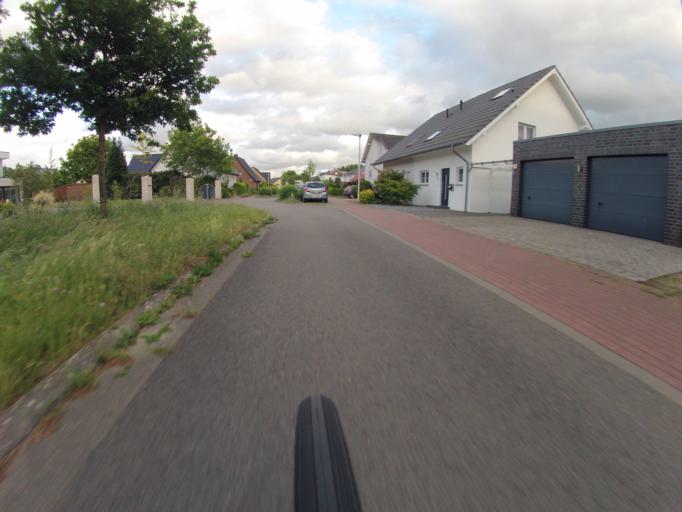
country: DE
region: North Rhine-Westphalia
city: Ibbenburen
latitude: 52.2819
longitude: 7.6924
